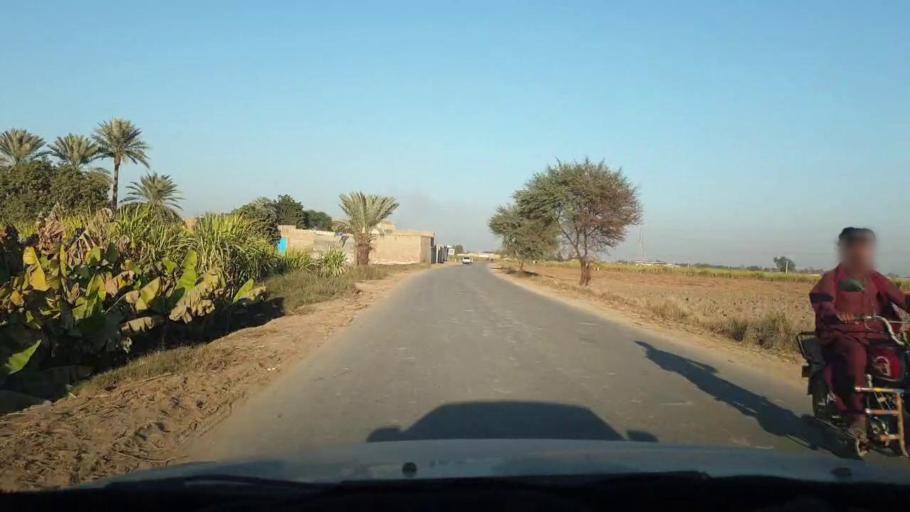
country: PK
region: Sindh
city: Ghotki
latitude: 27.9961
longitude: 69.2771
